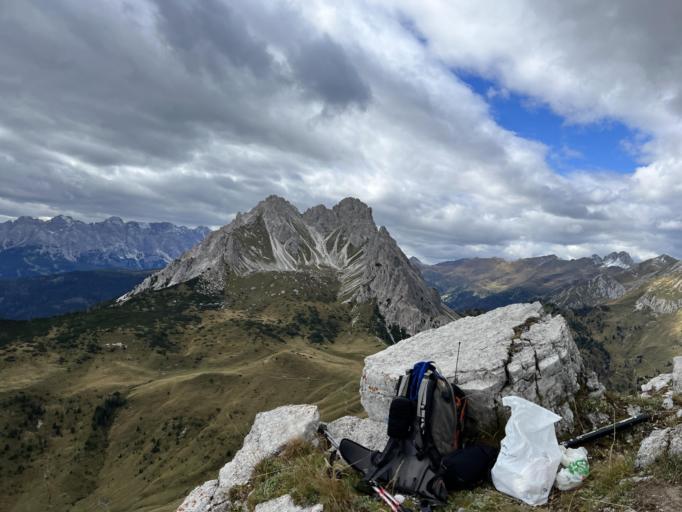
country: IT
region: Veneto
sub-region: Provincia di Belluno
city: San Pietro di Cadore
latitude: 46.6210
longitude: 12.5915
